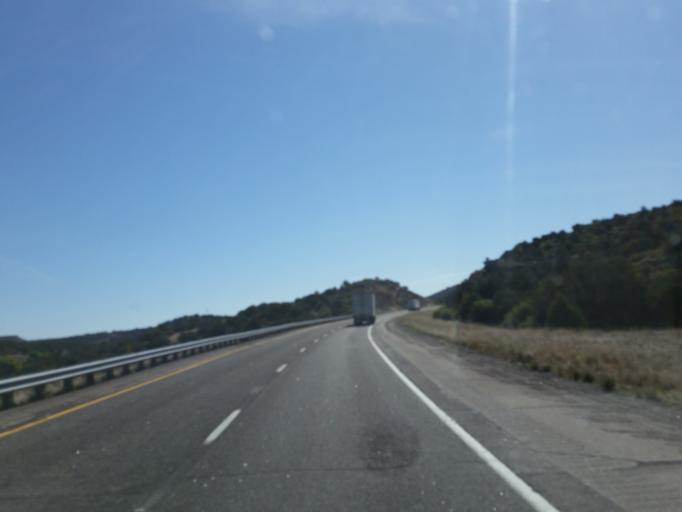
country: US
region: Arizona
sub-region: Mohave County
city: Peach Springs
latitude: 35.1803
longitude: -113.4695
